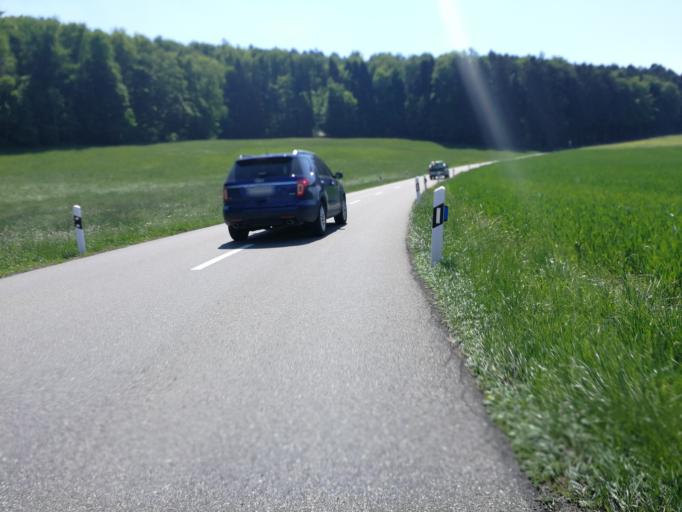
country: CH
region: Zurich
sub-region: Bezirk Uster
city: Aesch
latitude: 47.3205
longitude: 8.6525
